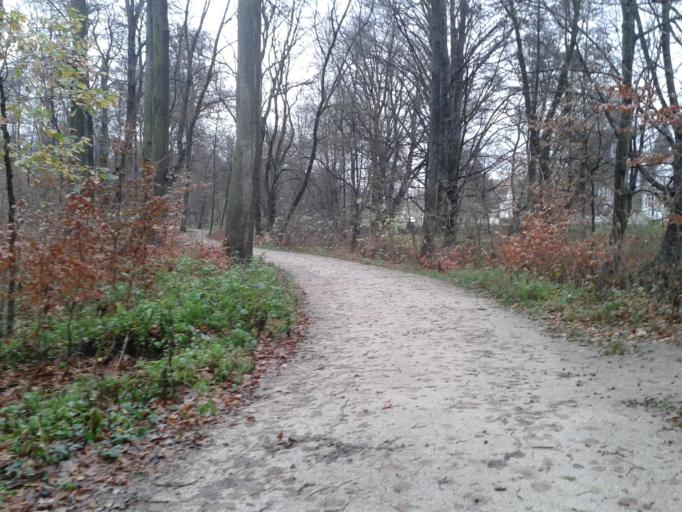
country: DE
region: Bavaria
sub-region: Upper Franconia
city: Bamberg
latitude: 49.8817
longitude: 10.8983
